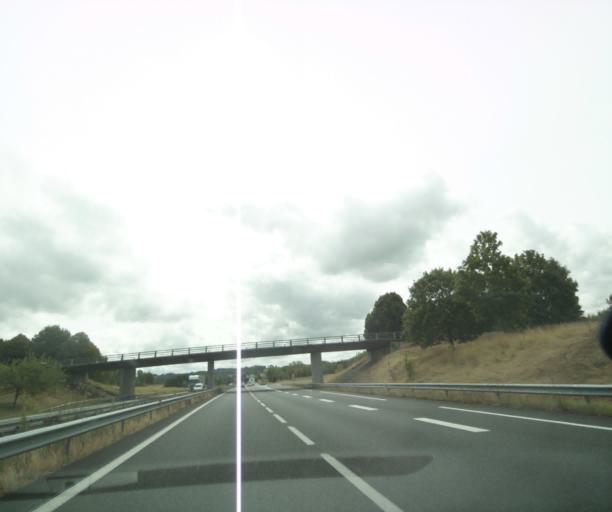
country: FR
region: Poitou-Charentes
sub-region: Departement de la Charente-Maritime
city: Mirambeau
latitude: 45.3719
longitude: -0.5937
